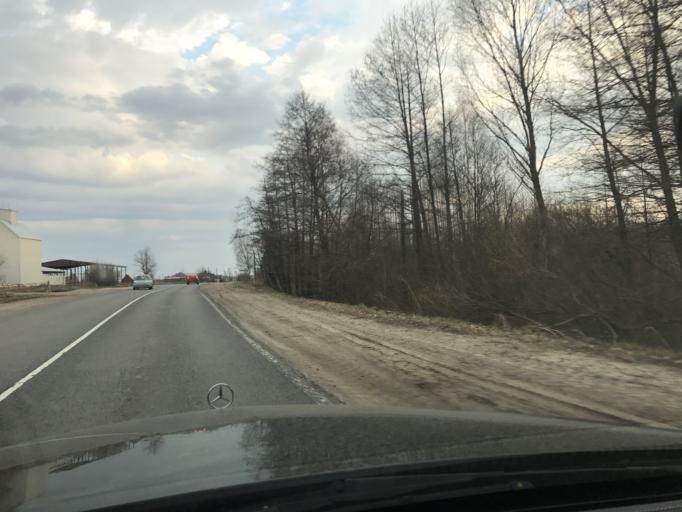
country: RU
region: Vladimir
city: Krasnaya Gorbatka
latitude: 55.6533
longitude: 41.8242
